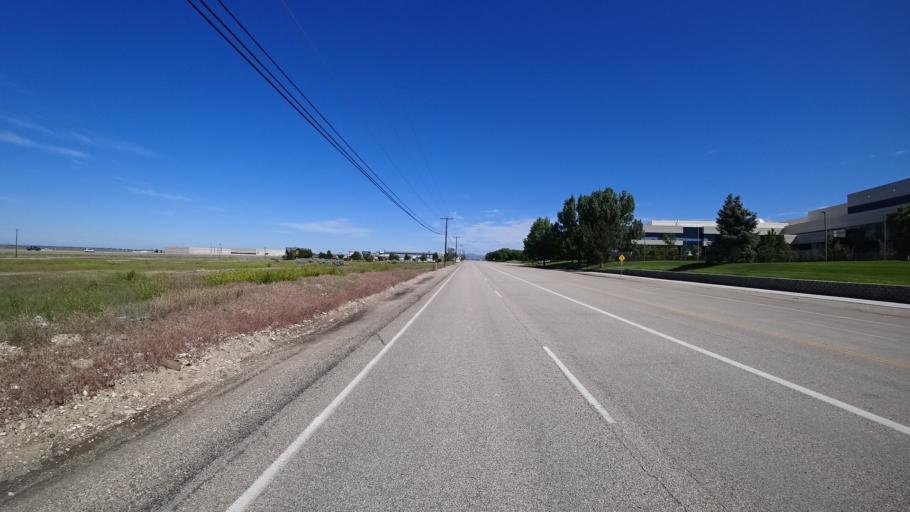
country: US
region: Idaho
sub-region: Ada County
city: Boise
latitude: 43.5292
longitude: -116.1506
